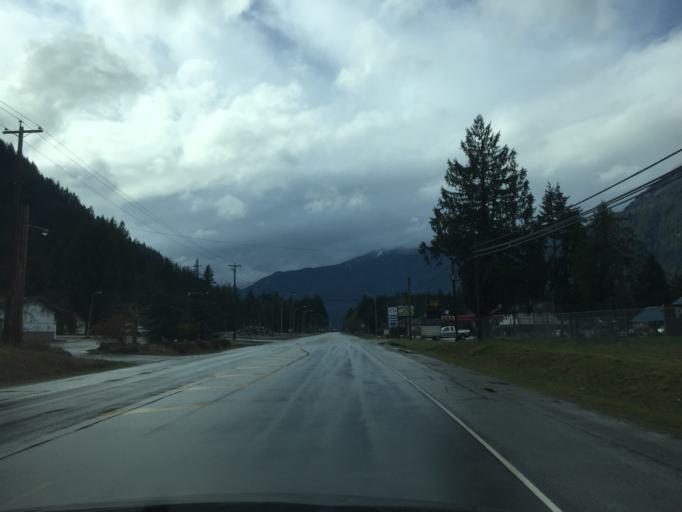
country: CA
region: British Columbia
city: Hope
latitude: 49.3604
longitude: -121.4646
